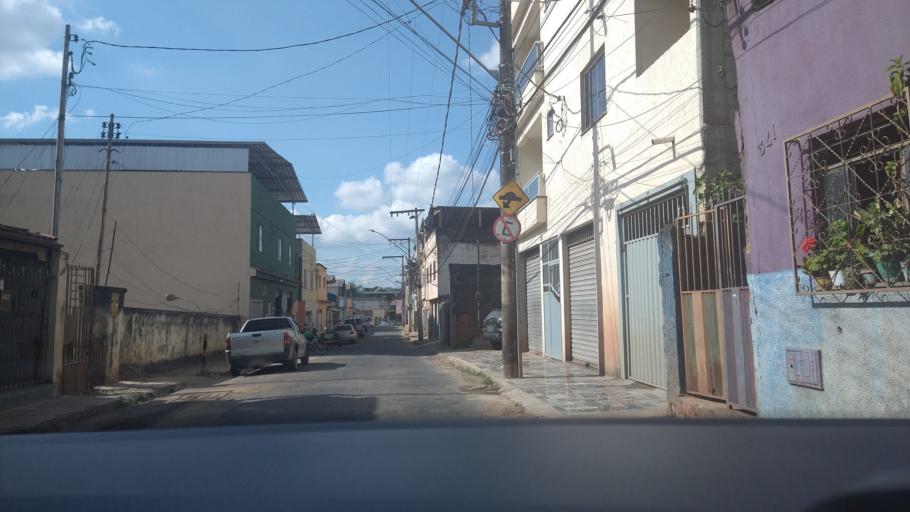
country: BR
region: Minas Gerais
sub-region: Vicosa
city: Vicosa
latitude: -20.7669
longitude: -42.8860
